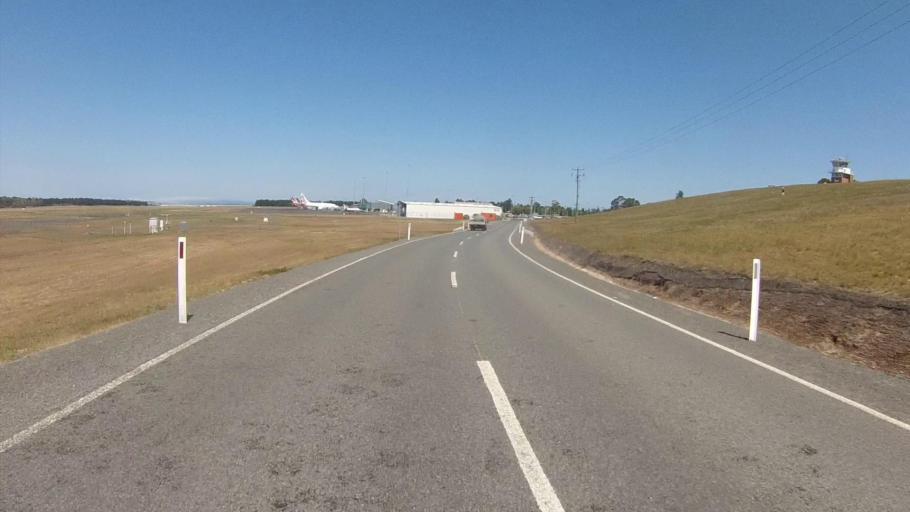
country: AU
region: Tasmania
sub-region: Clarence
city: Seven Mile Beach
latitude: -42.8334
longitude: 147.5022
